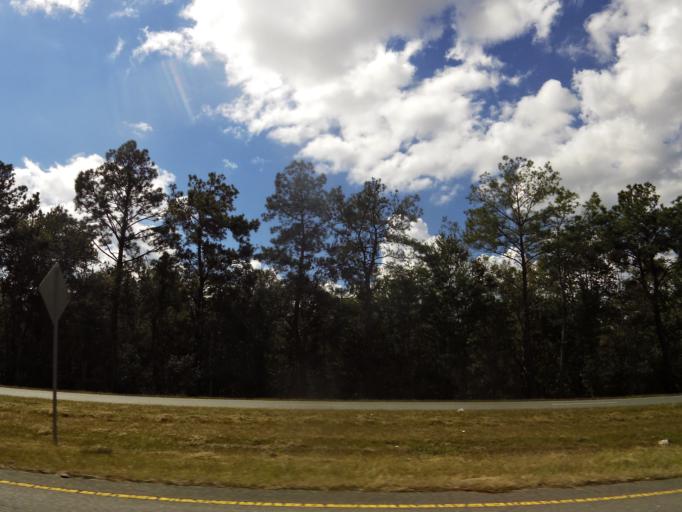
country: US
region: Georgia
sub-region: Charlton County
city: Folkston
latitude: 30.8020
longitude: -81.9904
